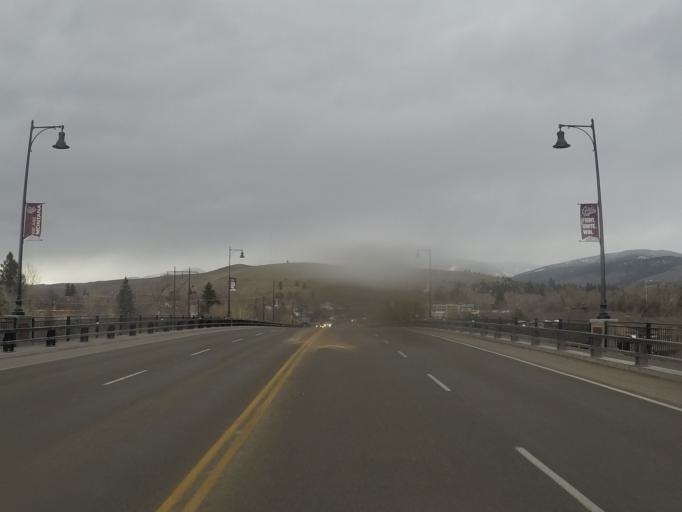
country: US
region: Montana
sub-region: Missoula County
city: Missoula
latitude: 46.8674
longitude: -113.9878
